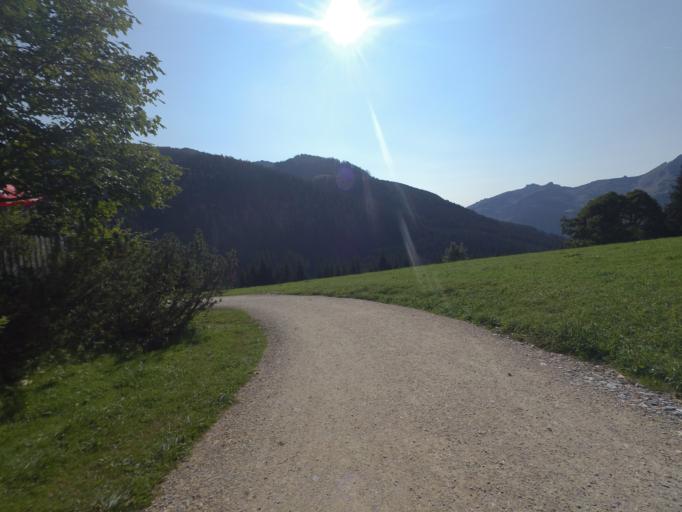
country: AT
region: Salzburg
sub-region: Politischer Bezirk Sankt Johann im Pongau
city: Kleinarl
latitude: 47.2734
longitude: 13.2521
